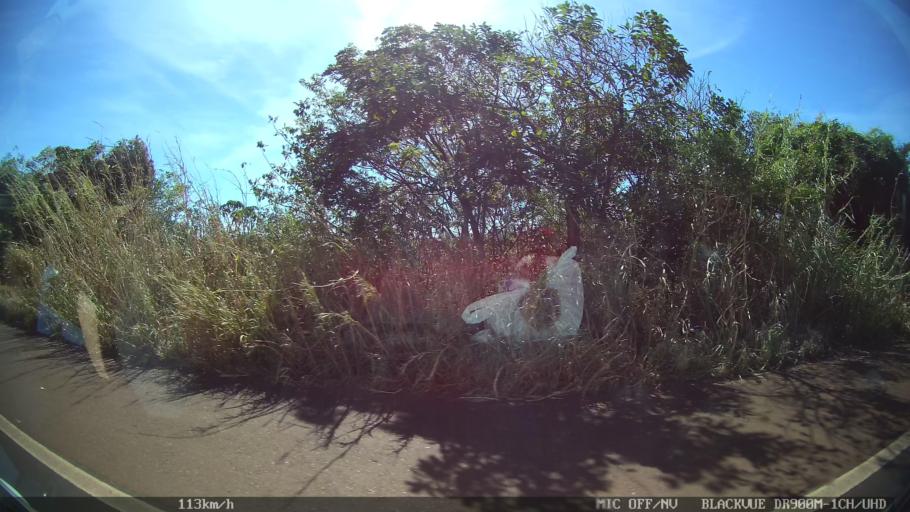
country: BR
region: Sao Paulo
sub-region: Nuporanga
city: Nuporanga
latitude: -20.5617
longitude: -47.6181
